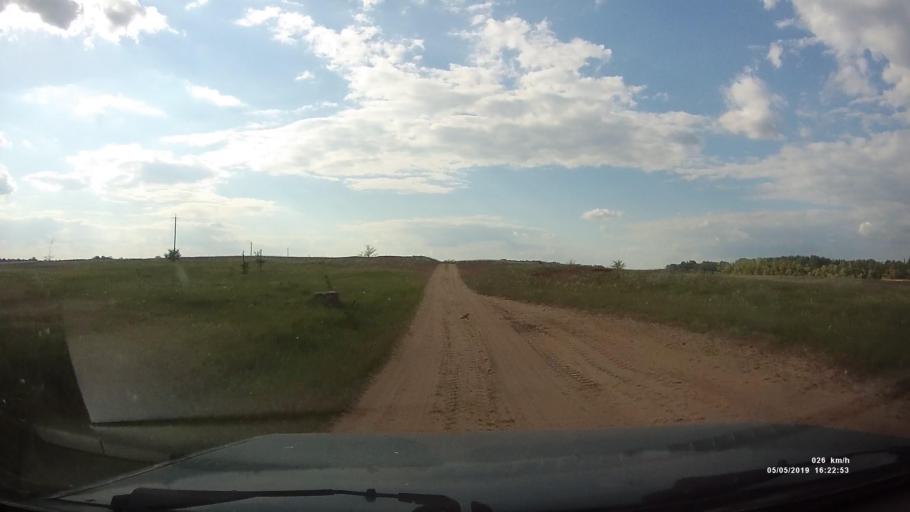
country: RU
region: Rostov
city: Konstantinovsk
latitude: 47.7549
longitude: 41.0331
